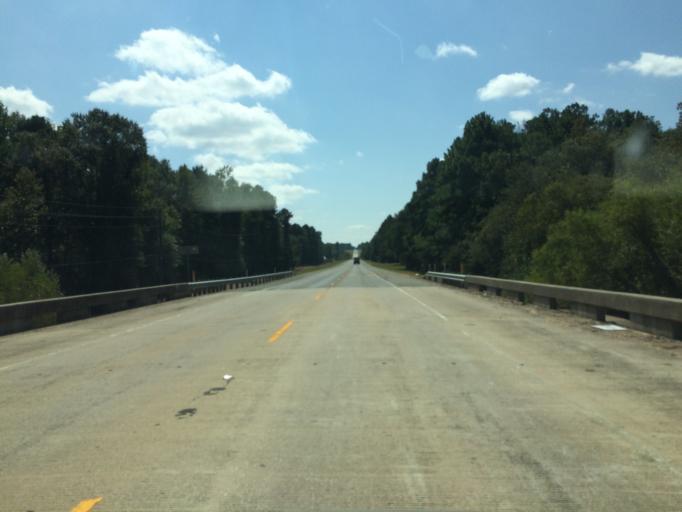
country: US
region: Texas
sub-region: Wood County
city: Hawkins
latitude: 32.7107
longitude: -95.2038
